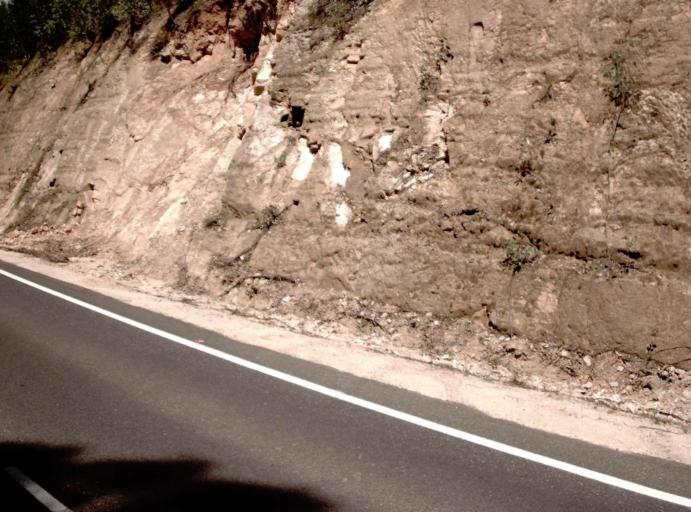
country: AU
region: New South Wales
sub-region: Bombala
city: Bombala
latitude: -37.5841
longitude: 148.9963
